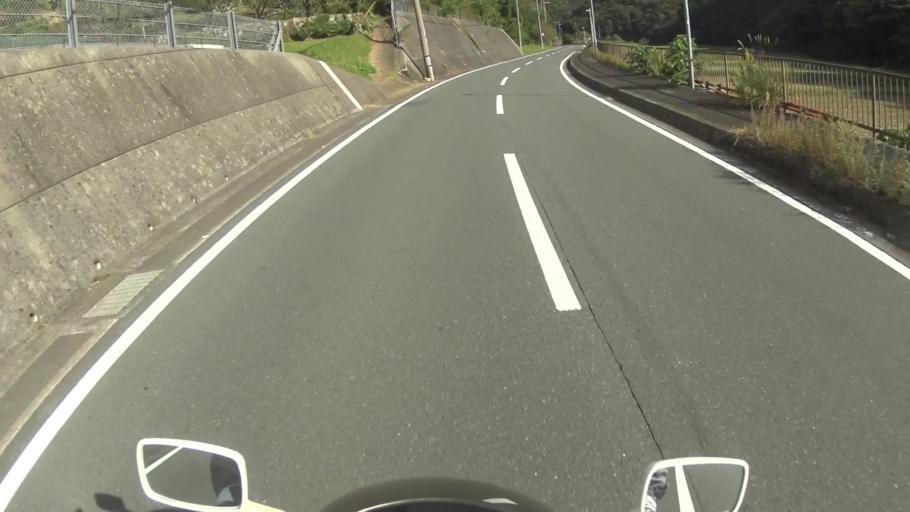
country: JP
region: Kyoto
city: Maizuru
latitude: 35.5211
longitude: 135.3584
